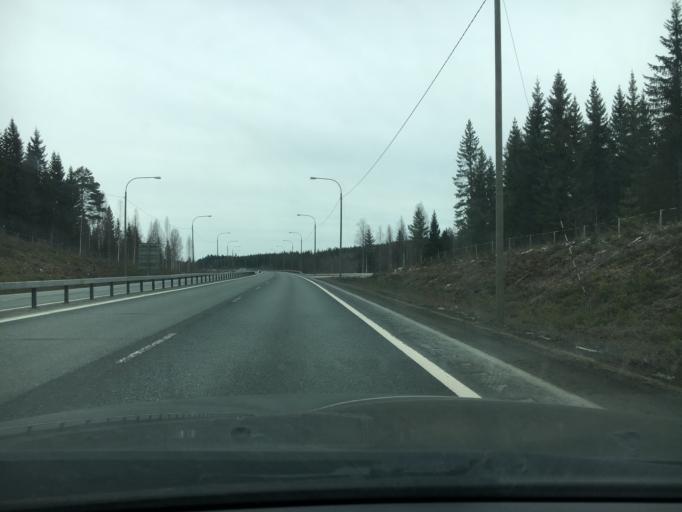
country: FI
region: Northern Savo
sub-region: Kuopio
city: Kuopio
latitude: 62.7309
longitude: 27.5860
